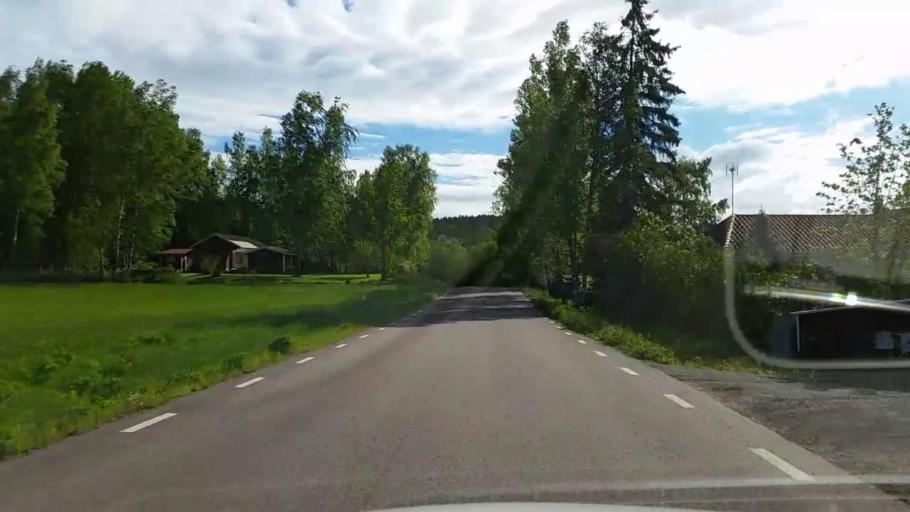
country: SE
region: Dalarna
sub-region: Borlange Kommun
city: Ornas
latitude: 60.5124
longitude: 15.5592
